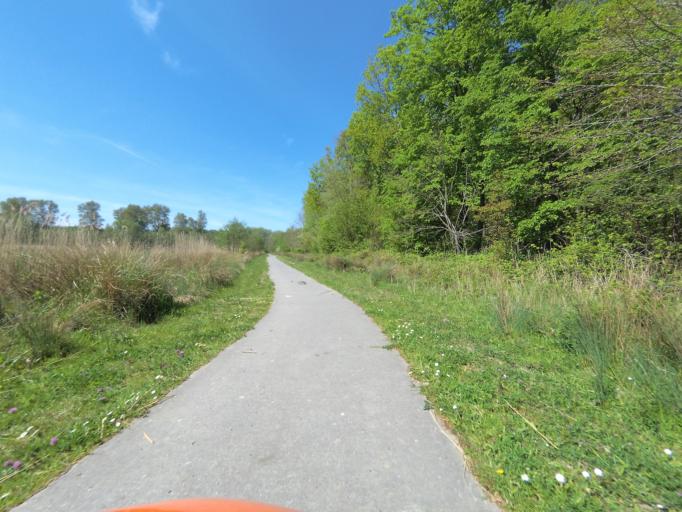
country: NL
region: Gelderland
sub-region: Gemeente Harderwijk
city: Harderwijk
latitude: 52.3892
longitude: 5.6245
